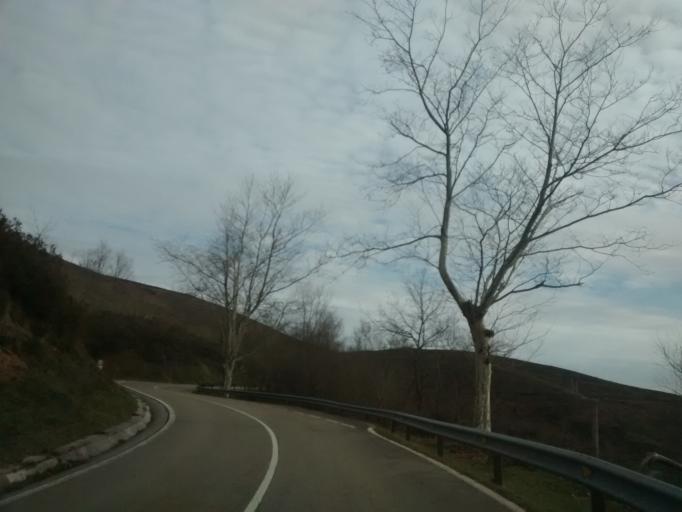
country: ES
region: Cantabria
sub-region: Provincia de Cantabria
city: Ruente
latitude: 43.2481
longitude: -4.3300
